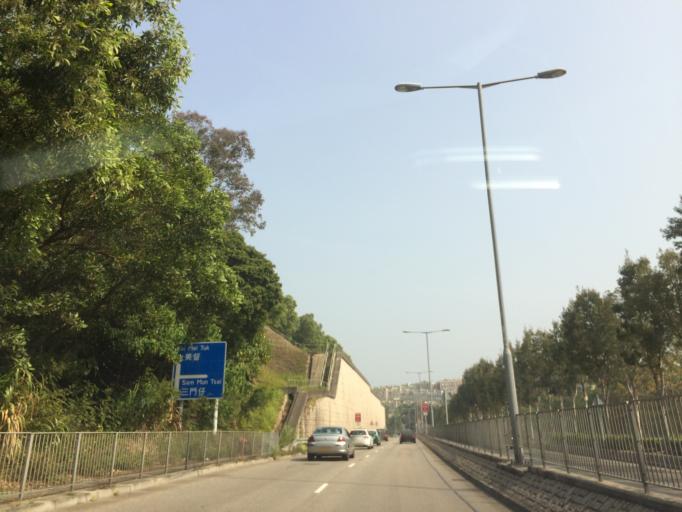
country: HK
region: Tai Po
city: Tai Po
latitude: 22.4600
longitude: 114.2005
